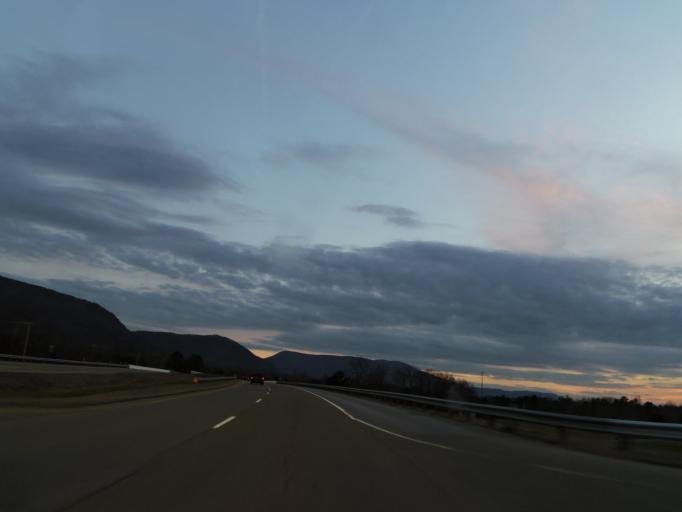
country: US
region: Tennessee
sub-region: McMinn County
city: Etowah
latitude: 35.2788
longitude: -84.5470
